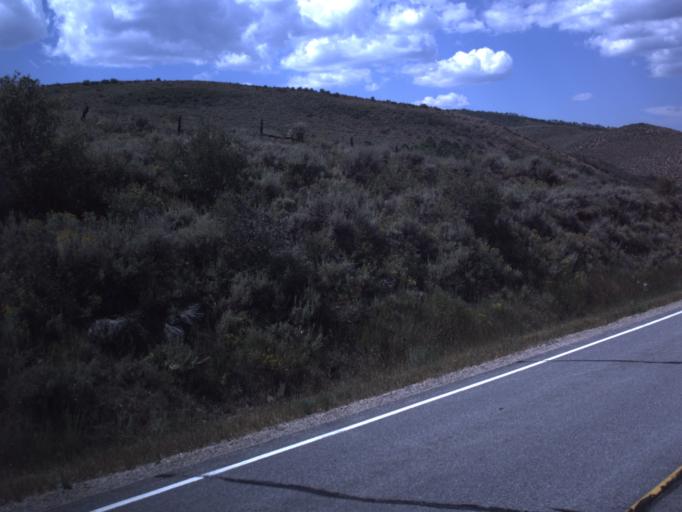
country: US
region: Utah
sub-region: Rich County
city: Randolph
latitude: 41.8146
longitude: -111.2688
